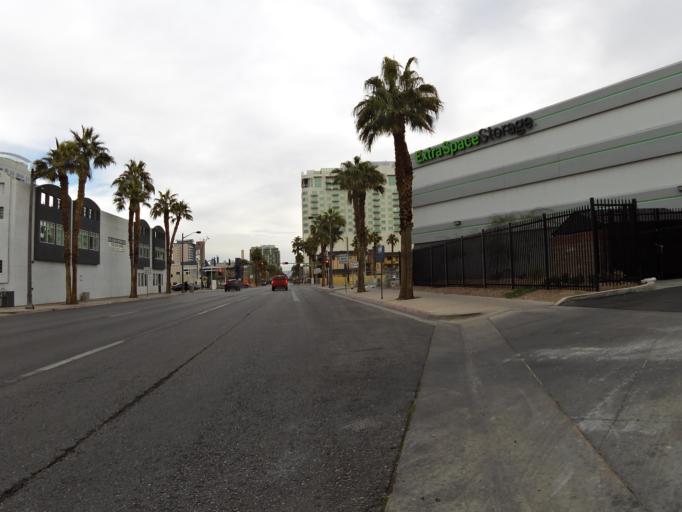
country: US
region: Nevada
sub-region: Clark County
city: Las Vegas
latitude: 36.1581
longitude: -115.1494
